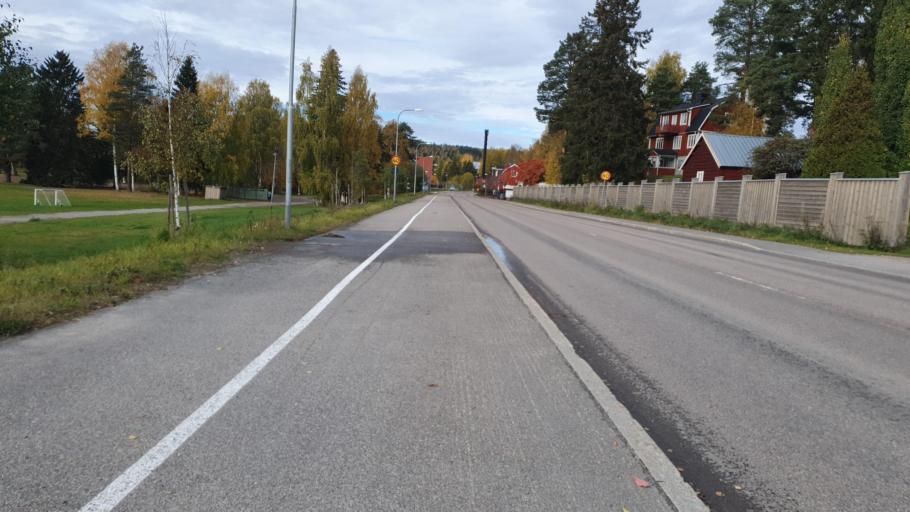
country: SE
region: Vaesternorrland
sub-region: Sundsvalls Kommun
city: Sundsvall
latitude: 62.4094
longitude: 17.2302
